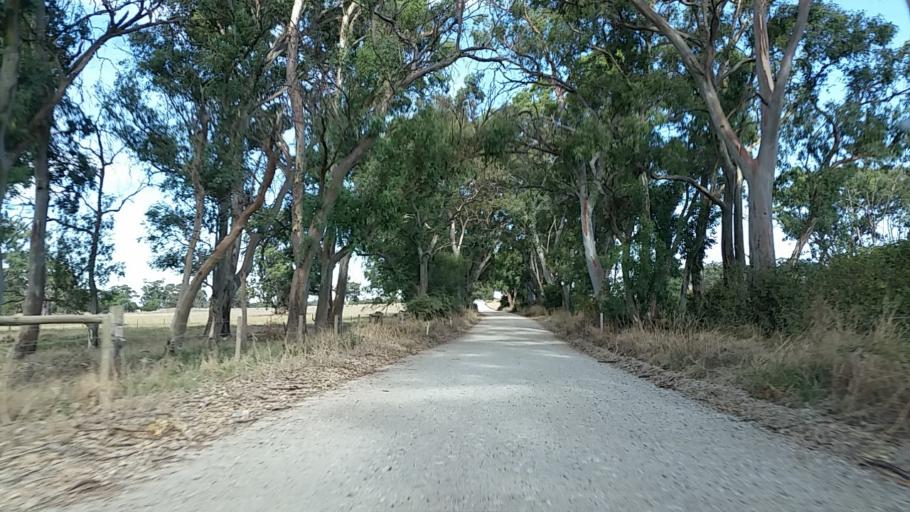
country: AU
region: South Australia
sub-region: Barossa
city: Angaston
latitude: -34.5710
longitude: 139.1141
